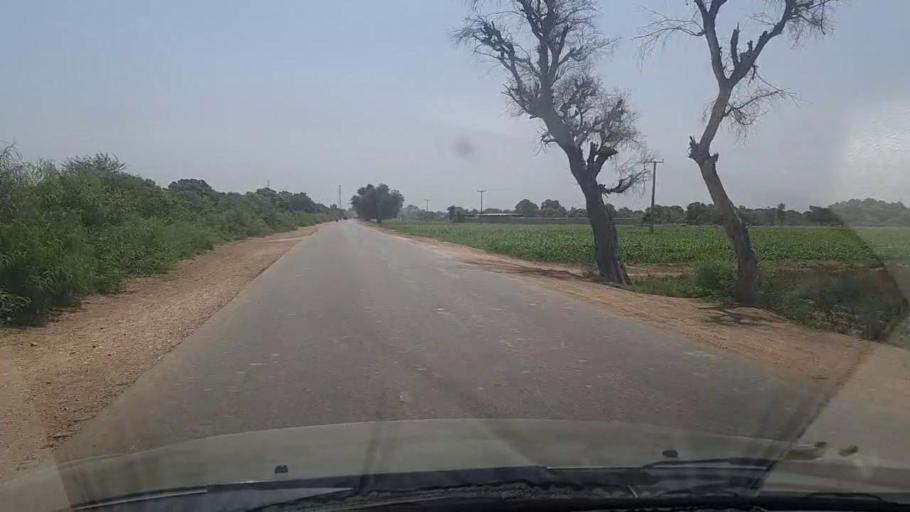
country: PK
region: Sindh
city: Tando Jam
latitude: 25.3612
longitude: 68.4929
